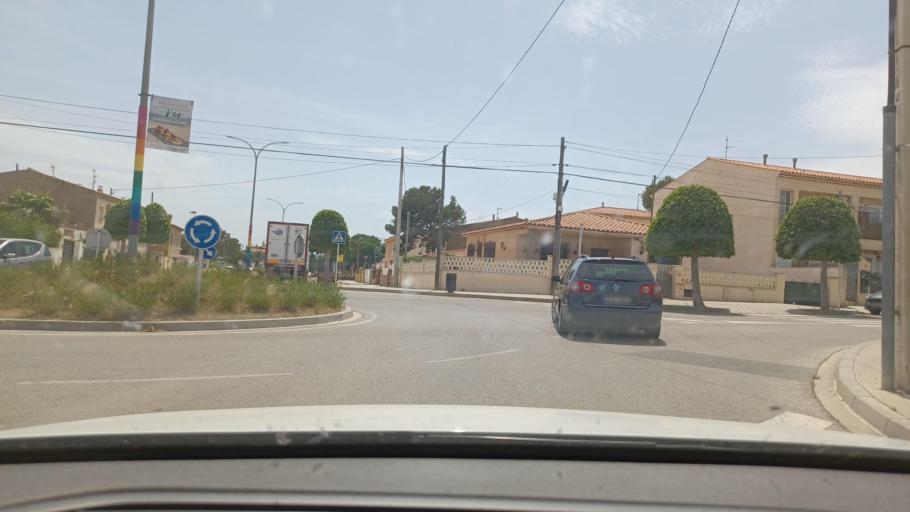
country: ES
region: Catalonia
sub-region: Provincia de Tarragona
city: Colldejou
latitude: 41.0059
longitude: 0.9282
